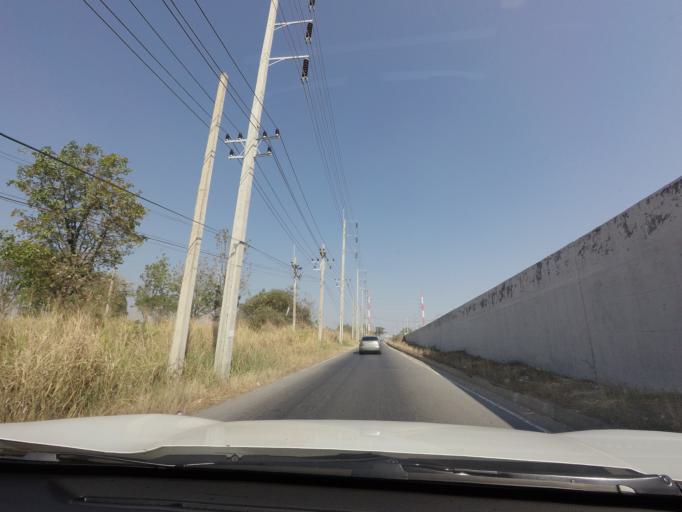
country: TH
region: Nakhon Ratchasima
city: Pak Chong
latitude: 14.6754
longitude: 101.4548
